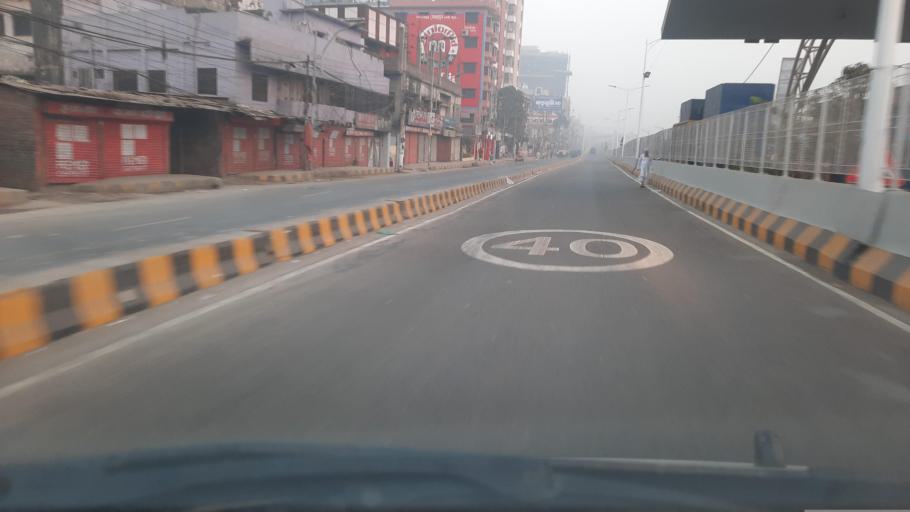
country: BD
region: Dhaka
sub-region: Dhaka
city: Dhaka
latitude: 23.7042
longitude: 90.4350
